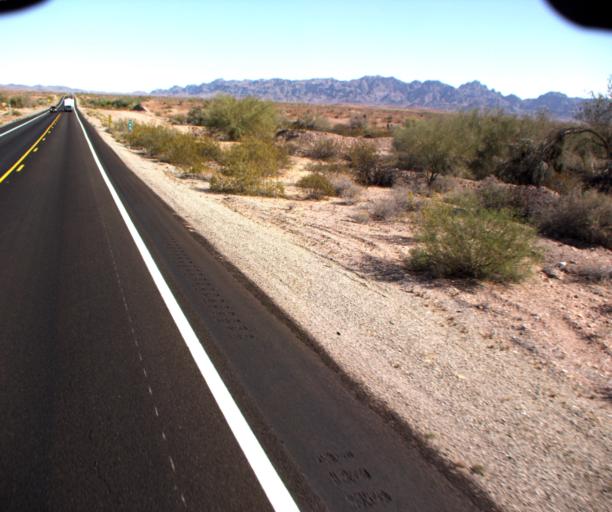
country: US
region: Arizona
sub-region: Yuma County
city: Wellton
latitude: 33.1193
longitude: -114.2925
